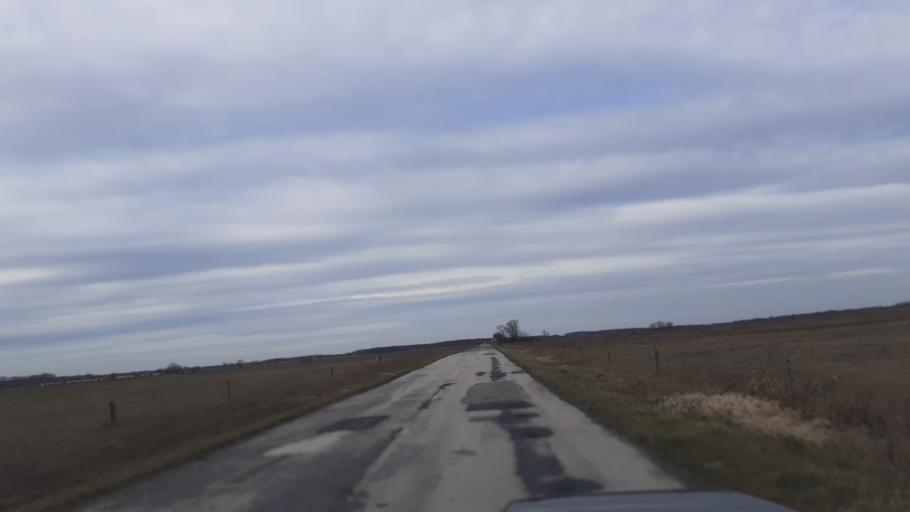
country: HU
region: Fejer
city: Sarbogard
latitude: 46.9158
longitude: 18.5582
